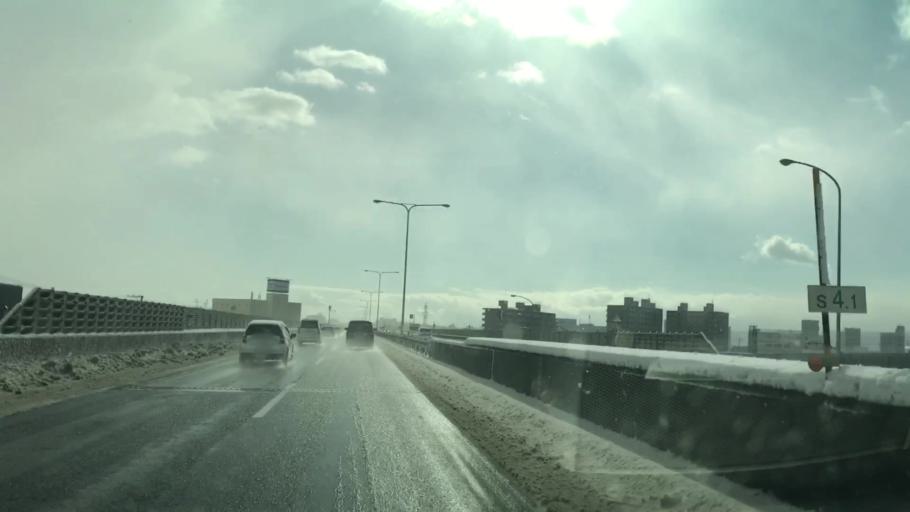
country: JP
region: Hokkaido
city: Sapporo
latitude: 43.0424
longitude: 141.4373
